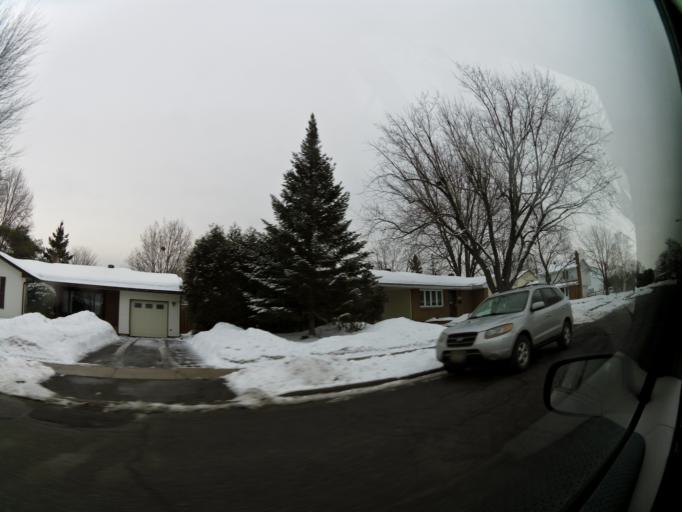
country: CA
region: Quebec
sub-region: Outaouais
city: Gatineau
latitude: 45.4566
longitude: -75.5949
